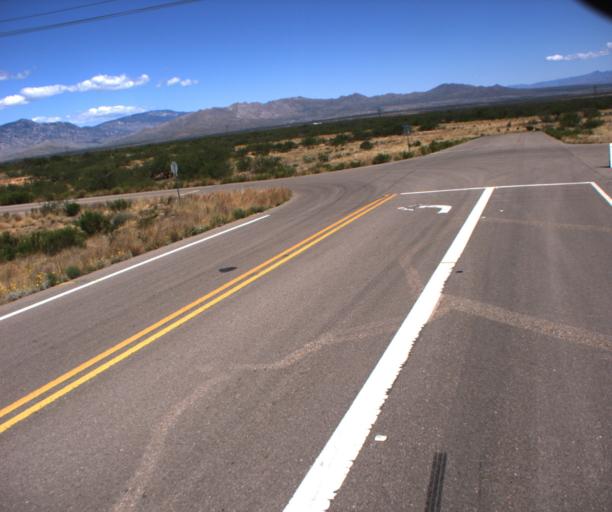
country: US
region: Arizona
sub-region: Cochise County
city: Whetstone
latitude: 31.9677
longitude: -110.3474
